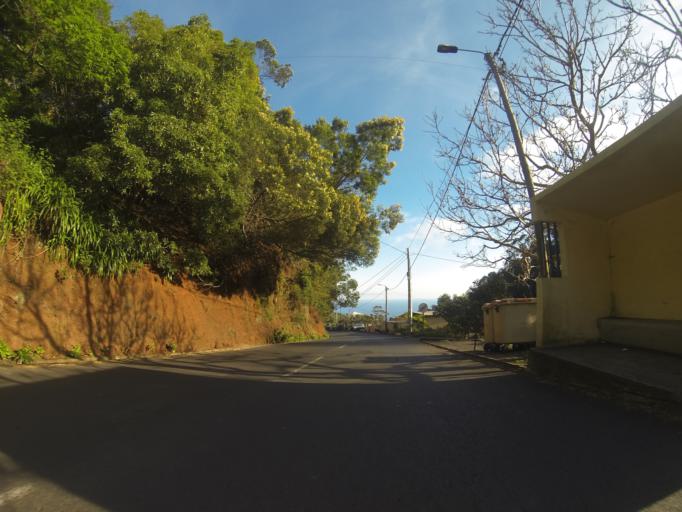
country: PT
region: Madeira
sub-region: Funchal
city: Nossa Senhora do Monte
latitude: 32.6645
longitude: -16.8723
